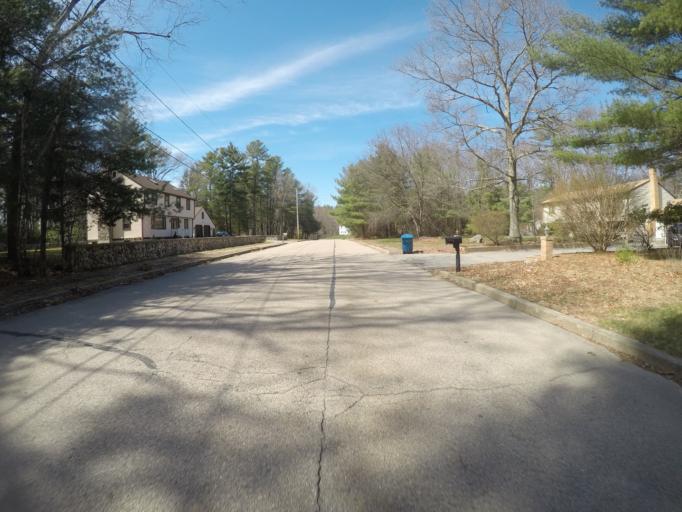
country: US
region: Massachusetts
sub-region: Bristol County
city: Easton
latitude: 42.0226
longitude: -71.0760
